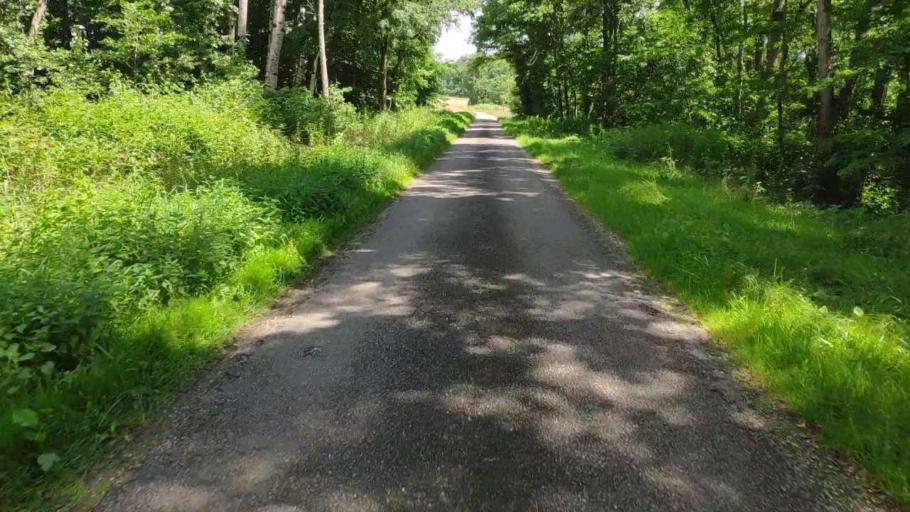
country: FR
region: Franche-Comte
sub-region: Departement du Jura
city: Chaussin
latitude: 46.8746
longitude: 5.4725
